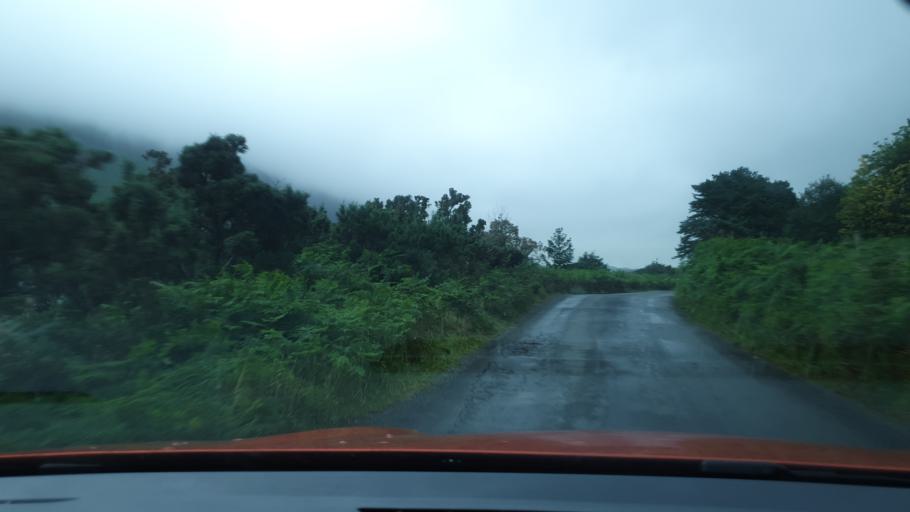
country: GB
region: England
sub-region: Cumbria
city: Seascale
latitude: 54.4503
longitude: -3.2835
